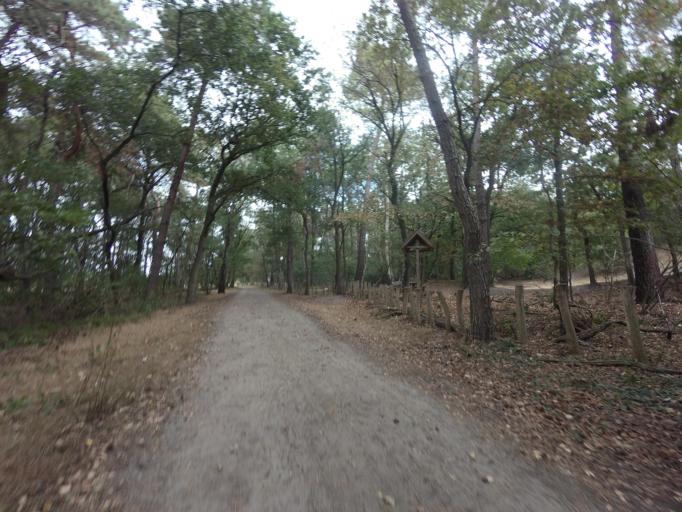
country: NL
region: North Brabant
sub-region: Gemeente Landerd
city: Zeeland
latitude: 51.7064
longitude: 5.6544
